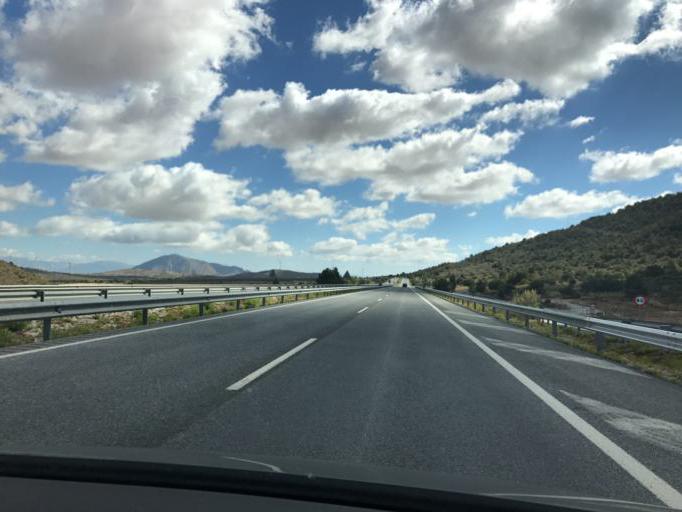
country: ES
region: Andalusia
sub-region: Provincia de Granada
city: Freila
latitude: 37.4632
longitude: -2.8686
